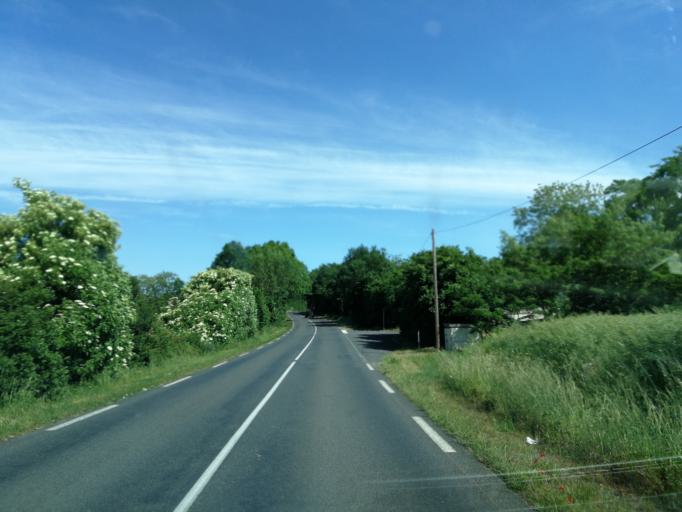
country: FR
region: Poitou-Charentes
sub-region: Departement des Deux-Sevres
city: Saint-Jean-de-Thouars
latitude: 46.9738
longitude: -0.1751
